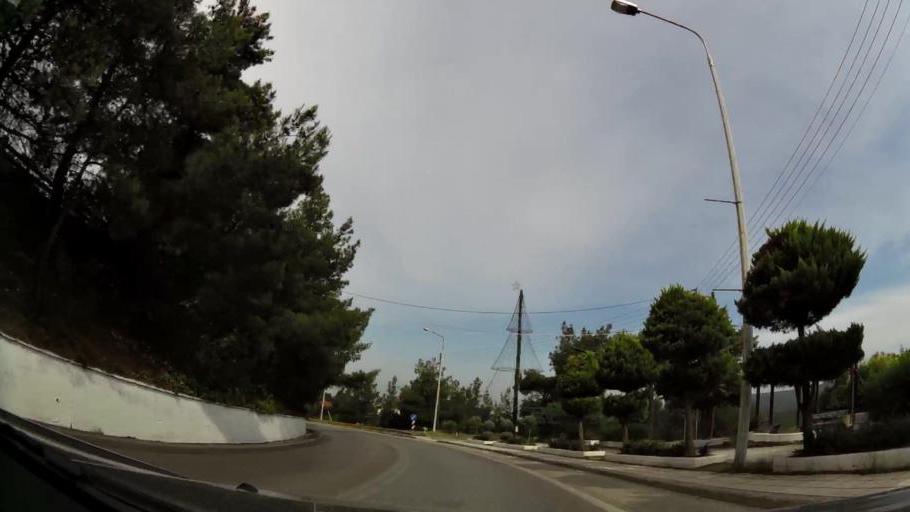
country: GR
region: Central Macedonia
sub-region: Nomos Thessalonikis
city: Panorama
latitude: 40.5922
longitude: 23.0311
